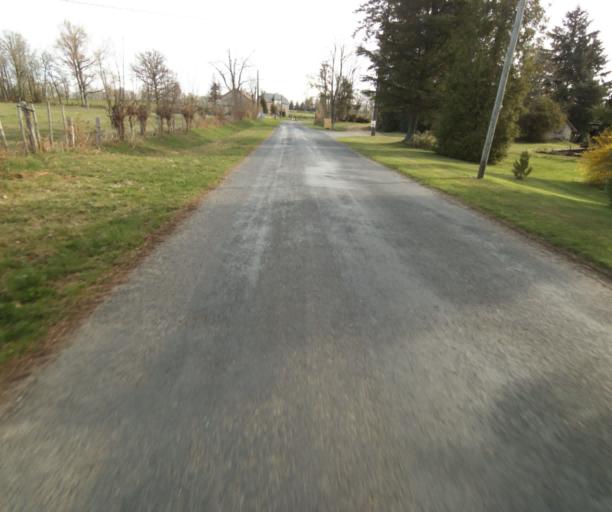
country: FR
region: Limousin
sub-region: Departement de la Correze
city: Chamboulive
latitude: 45.4374
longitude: 1.7751
